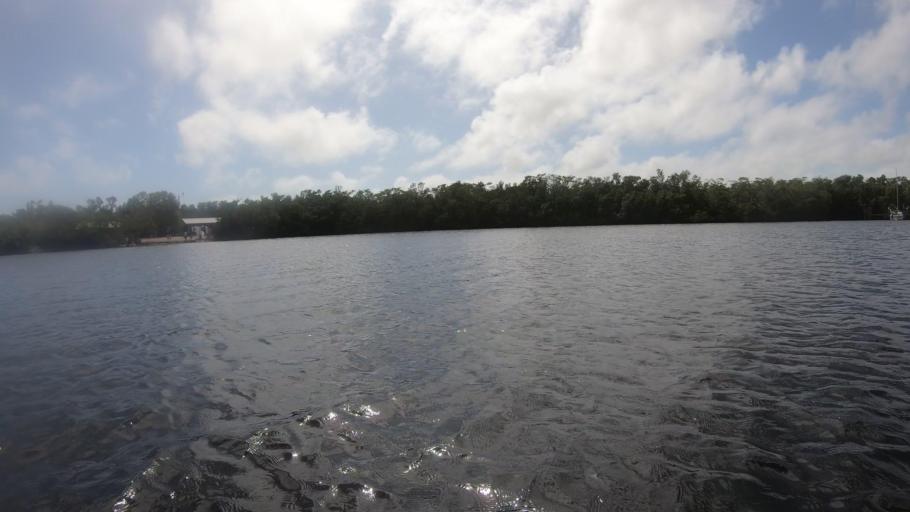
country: US
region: Florida
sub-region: Monroe County
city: Key Largo
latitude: 25.1236
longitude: -80.4060
